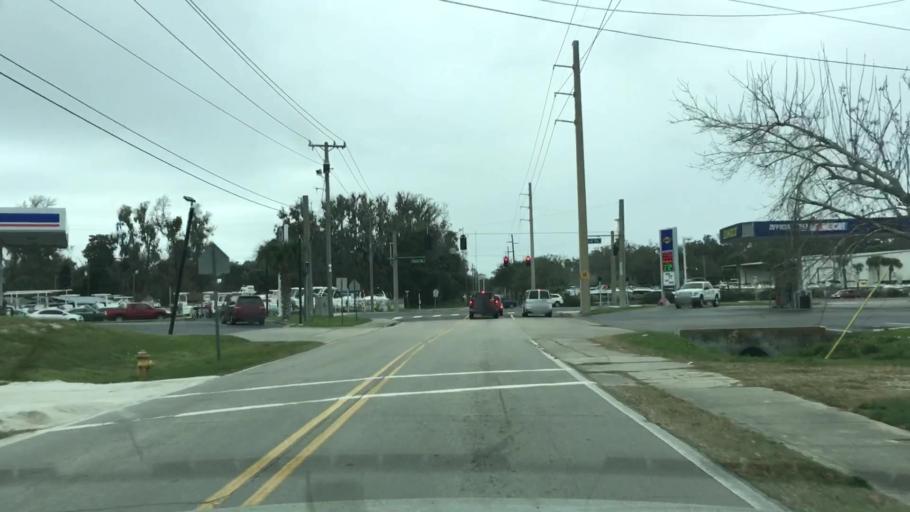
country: US
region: Florida
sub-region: Volusia County
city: Holly Hill
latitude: 29.2423
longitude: -81.0596
